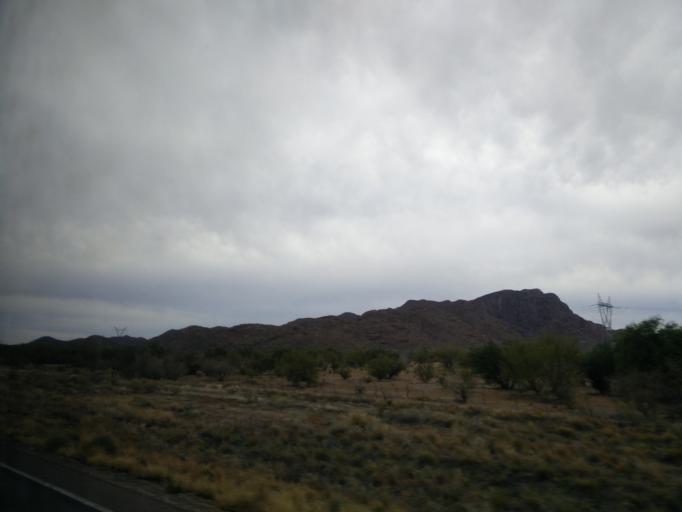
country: MX
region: Sonora
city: Hermosillo
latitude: 28.5965
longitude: -111.0229
